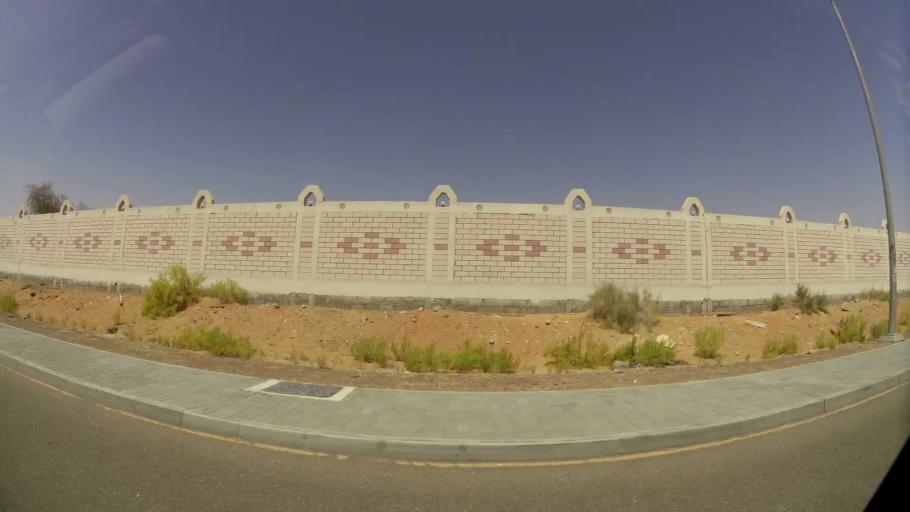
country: OM
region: Al Buraimi
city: Al Buraymi
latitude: 24.3016
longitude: 55.7629
